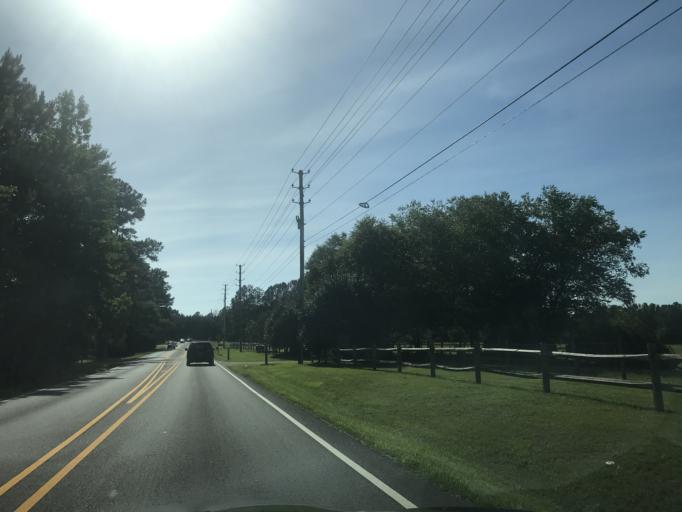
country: US
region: North Carolina
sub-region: Wake County
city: Garner
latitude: 35.6665
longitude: -78.5684
